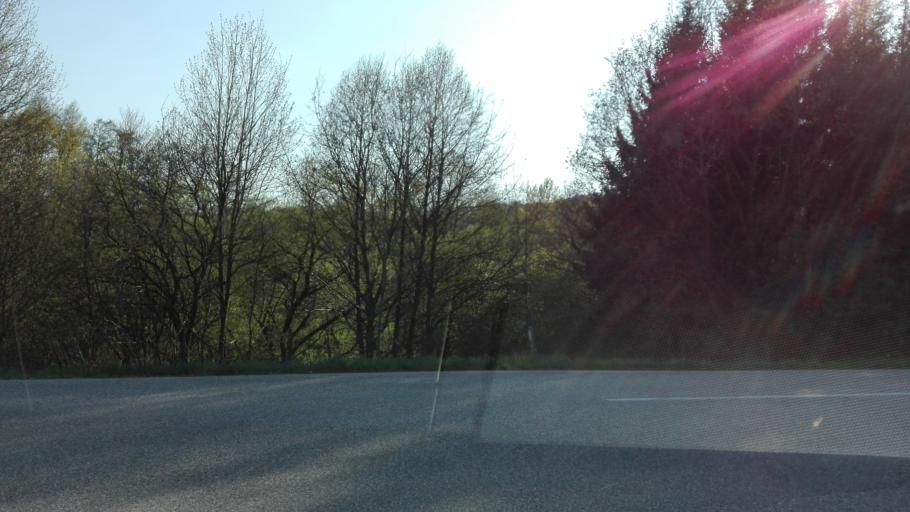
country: AT
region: Upper Austria
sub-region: Politischer Bezirk Grieskirchen
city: Grieskirchen
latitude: 48.3673
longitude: 13.7927
